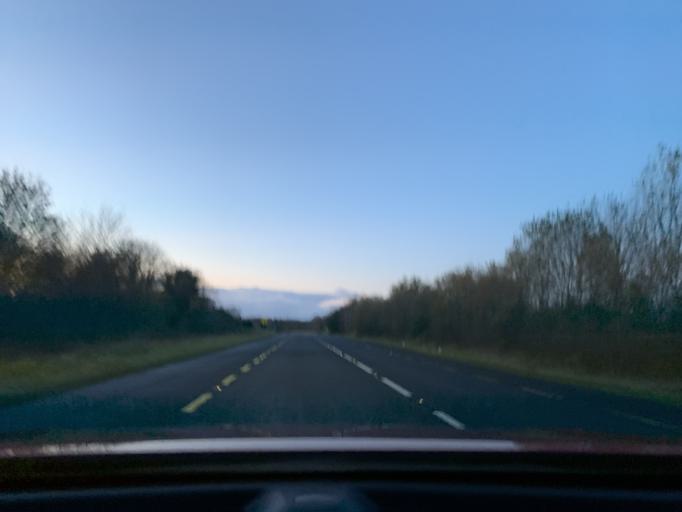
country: IE
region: Connaught
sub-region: County Leitrim
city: Carrick-on-Shannon
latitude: 53.9551
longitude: -8.1581
